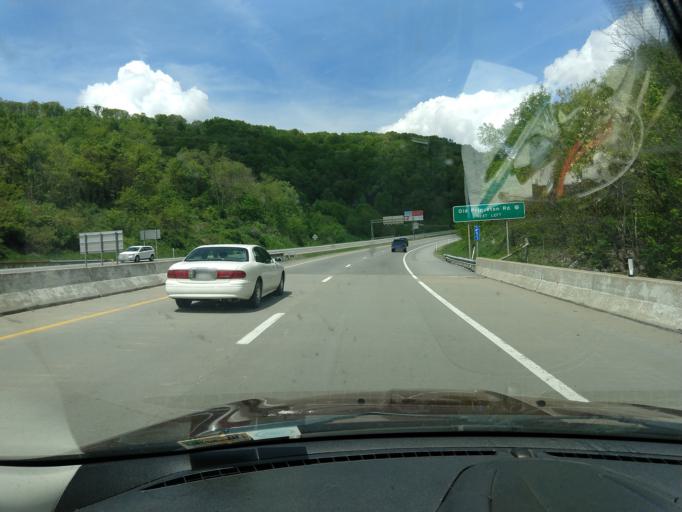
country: US
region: West Virginia
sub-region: Mercer County
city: Bluefield
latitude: 37.2849
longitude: -81.1669
